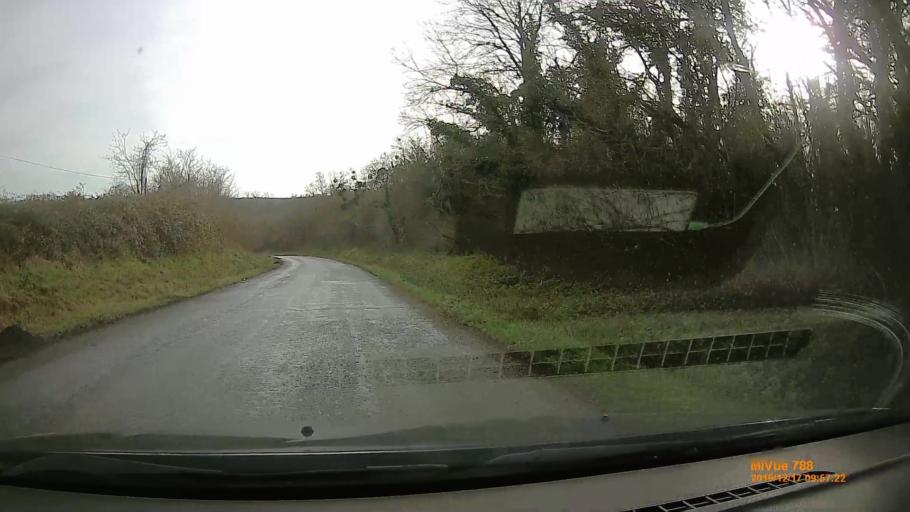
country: HU
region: Somogy
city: Karad
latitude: 46.6208
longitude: 17.7849
